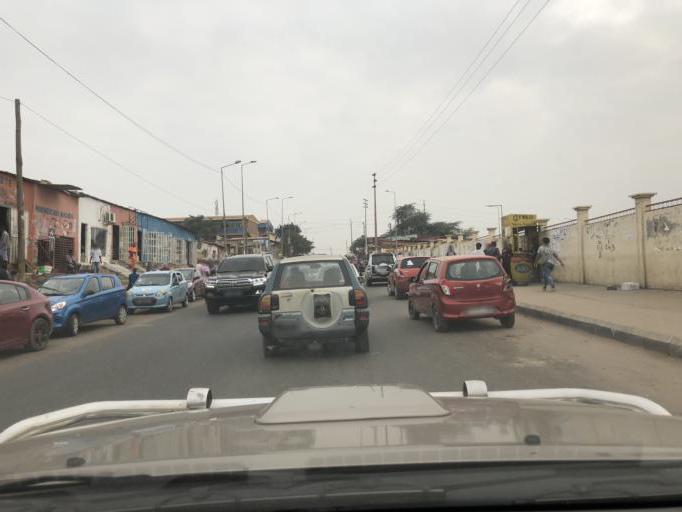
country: AO
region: Luanda
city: Luanda
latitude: -8.9009
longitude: 13.2149
